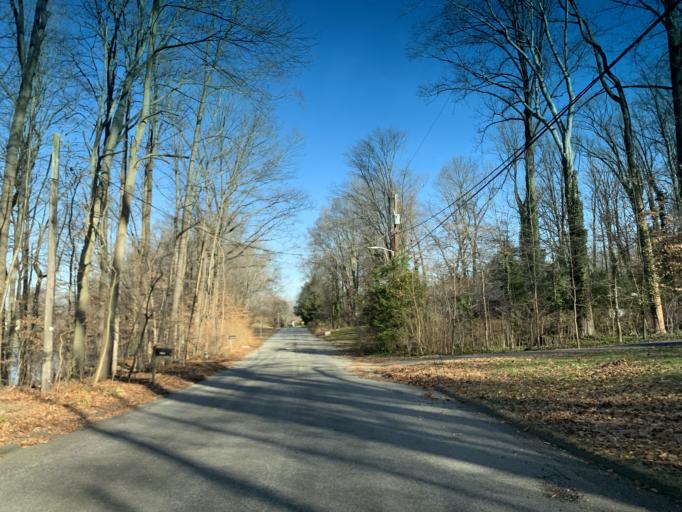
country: US
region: Maryland
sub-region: Harford County
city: South Bel Air
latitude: 39.5761
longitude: -76.2451
